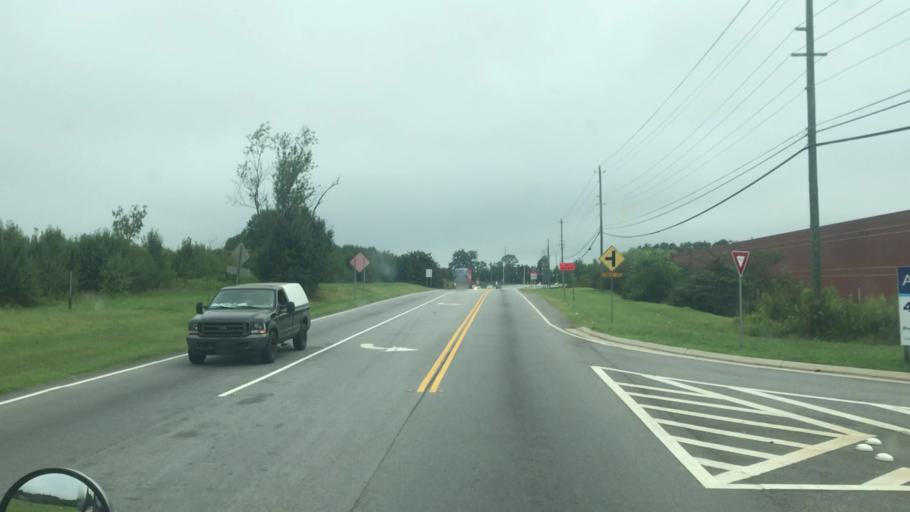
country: US
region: Georgia
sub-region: Henry County
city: McDonough
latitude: 33.3998
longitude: -84.1737
